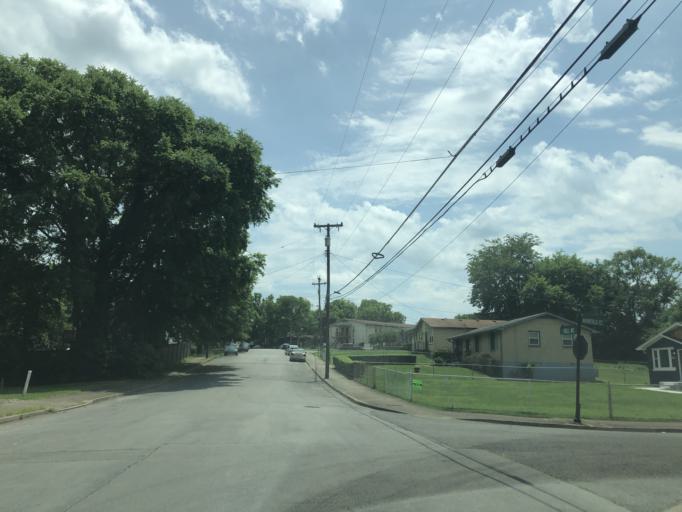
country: US
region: Tennessee
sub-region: Davidson County
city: Nashville
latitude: 36.1817
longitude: -86.7600
